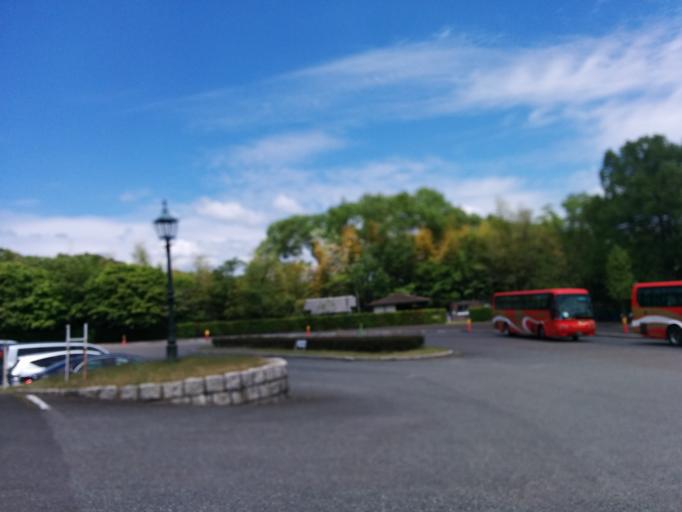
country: JP
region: Gifu
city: Inuyama
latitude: 35.3406
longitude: 136.9882
